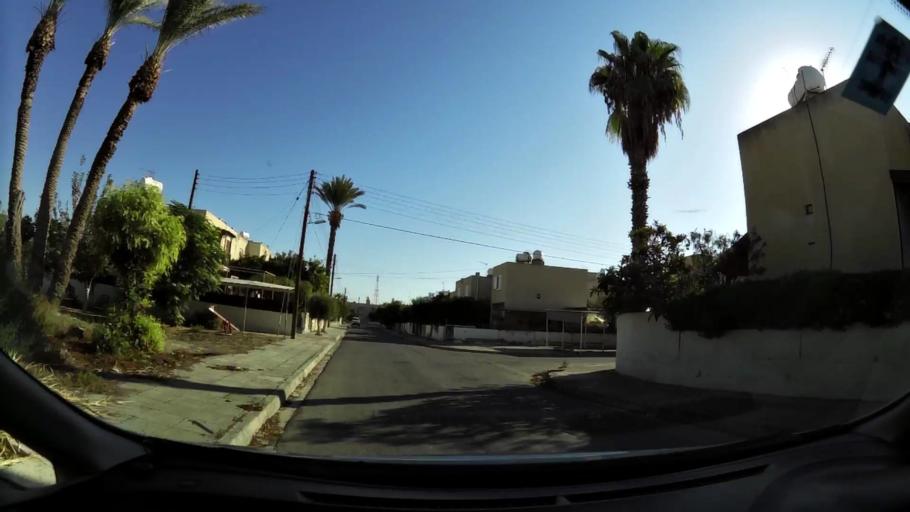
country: CY
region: Larnaka
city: Larnaca
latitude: 34.9279
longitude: 33.6196
